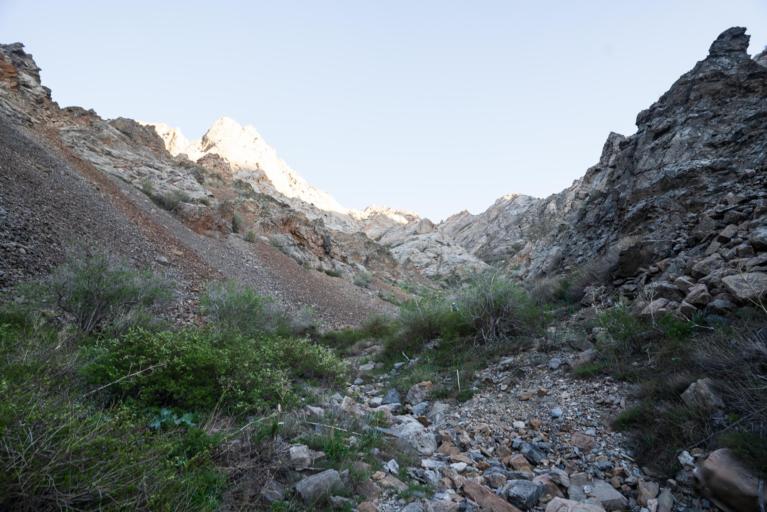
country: KZ
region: Ongtustik Qazaqstan
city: Ashchysay
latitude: 43.7681
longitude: 68.7772
